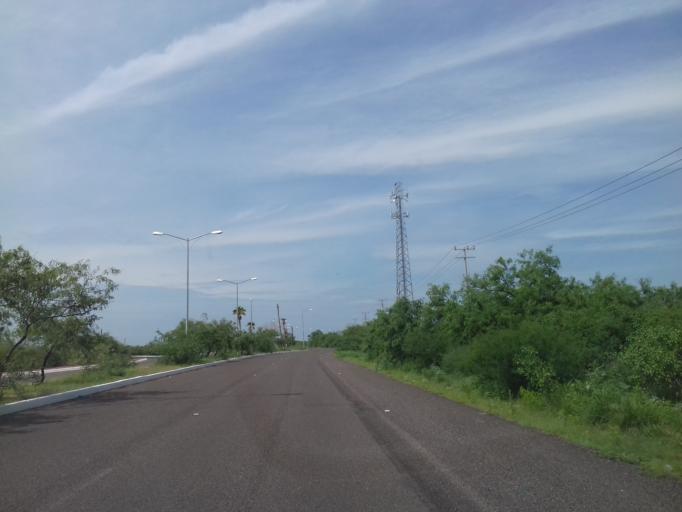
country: MX
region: Sonora
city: Heroica Guaymas
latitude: 27.9696
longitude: -111.1040
